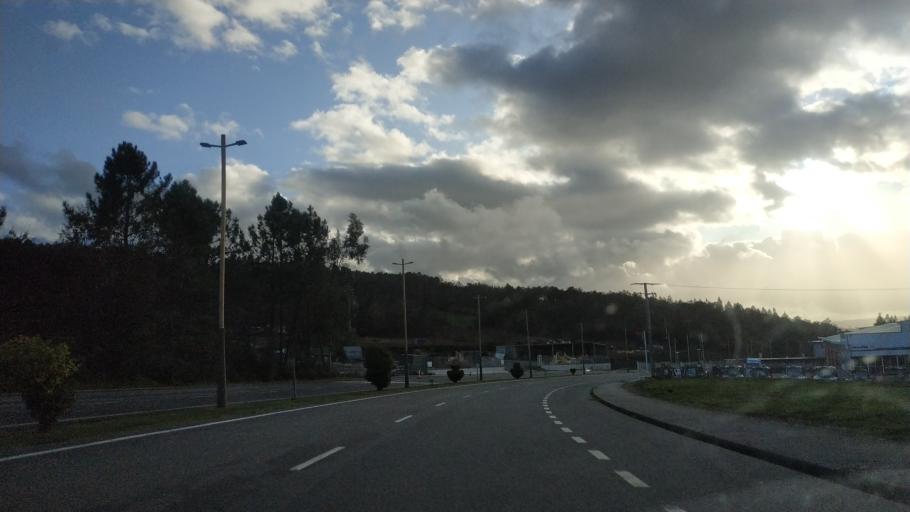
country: ES
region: Galicia
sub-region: Provincia de Pontevedra
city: Silleda
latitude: 42.7915
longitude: -8.1611
